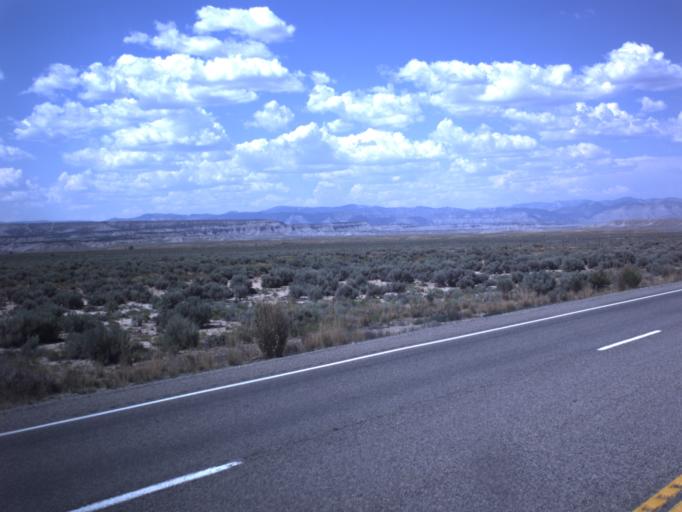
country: US
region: Utah
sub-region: Carbon County
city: Price
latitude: 39.4819
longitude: -110.8520
